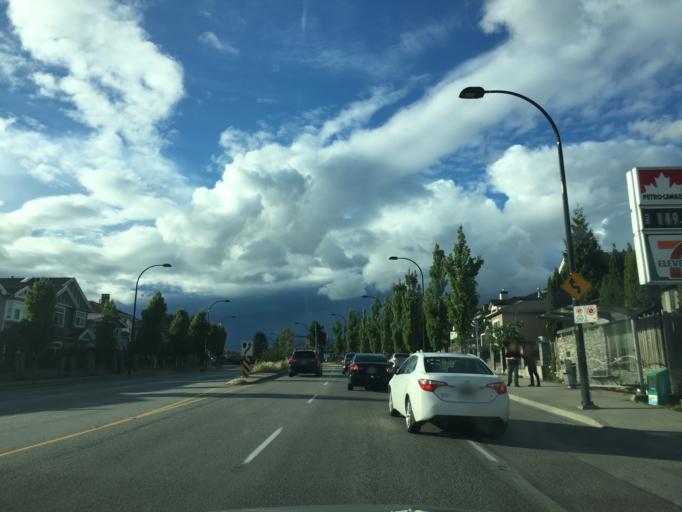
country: CA
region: British Columbia
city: Vancouver
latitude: 49.2183
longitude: -123.0769
